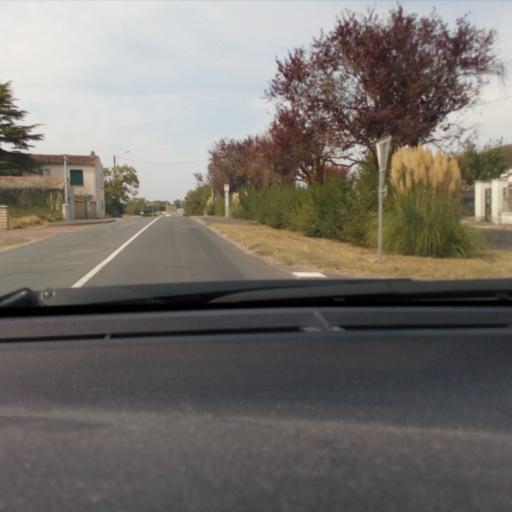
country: FR
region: Poitou-Charentes
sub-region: Departement de la Charente
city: Saint-Yrieix-sur-Charente
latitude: 45.6843
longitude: 0.1122
